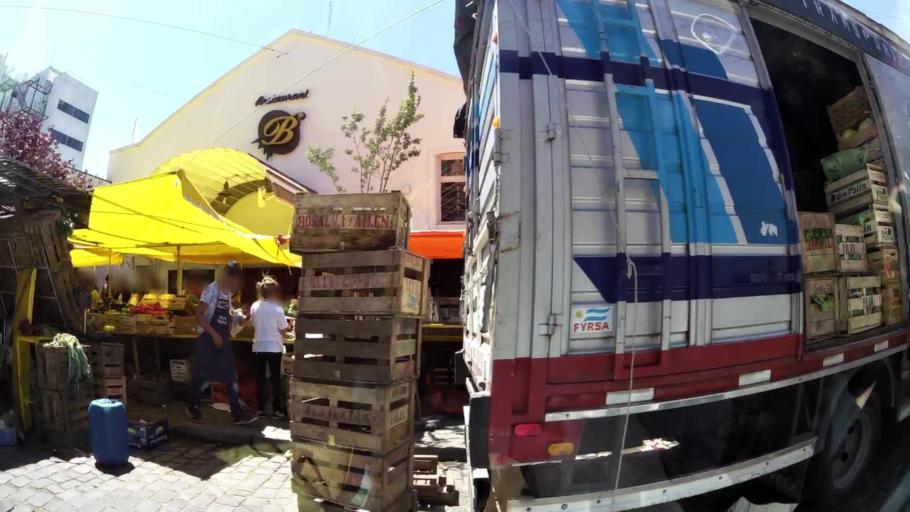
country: AR
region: Buenos Aires F.D.
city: Buenos Aires
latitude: -34.6155
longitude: -58.3705
